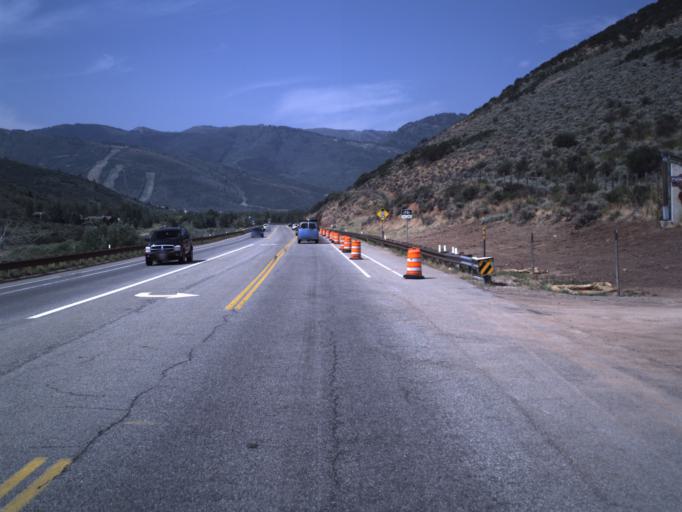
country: US
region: Utah
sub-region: Summit County
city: Park City
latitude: 40.6710
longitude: -111.4762
